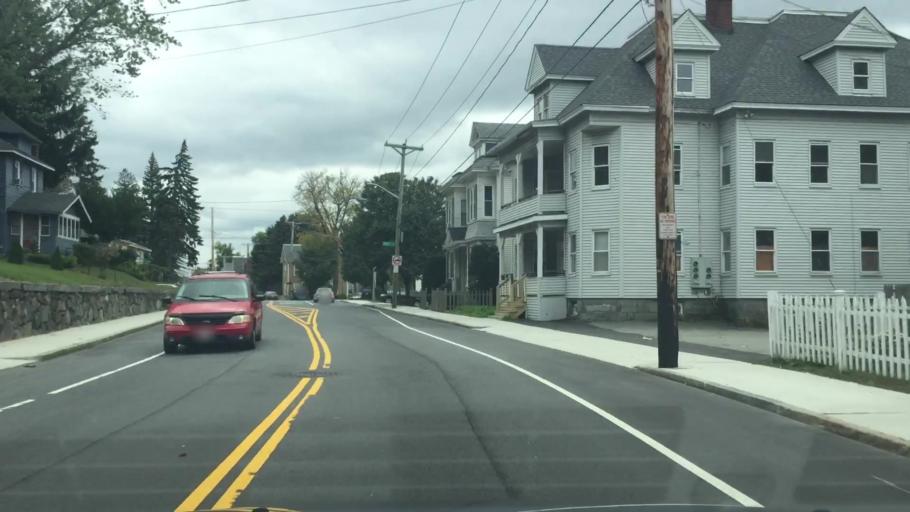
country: US
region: Massachusetts
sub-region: Middlesex County
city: Dracut
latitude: 42.6583
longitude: -71.3036
